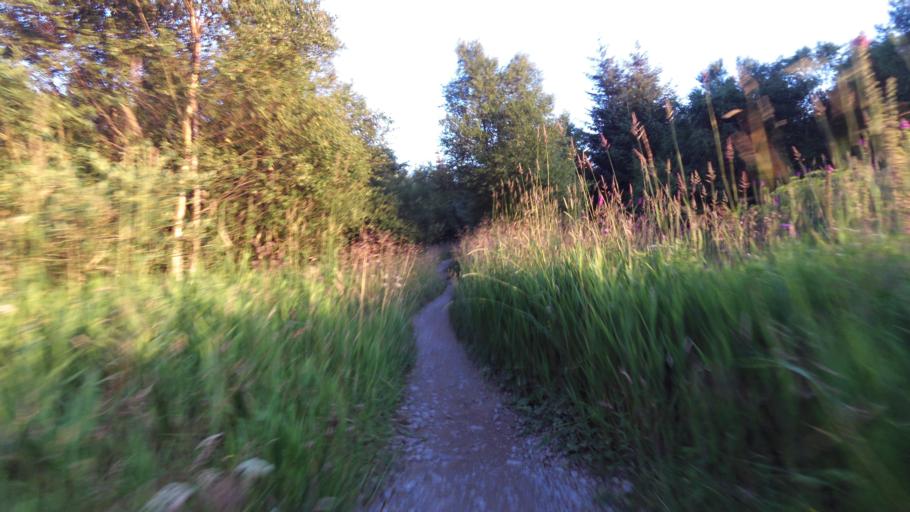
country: GB
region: England
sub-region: Lancashire
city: Clitheroe
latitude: 53.9973
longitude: -2.3876
